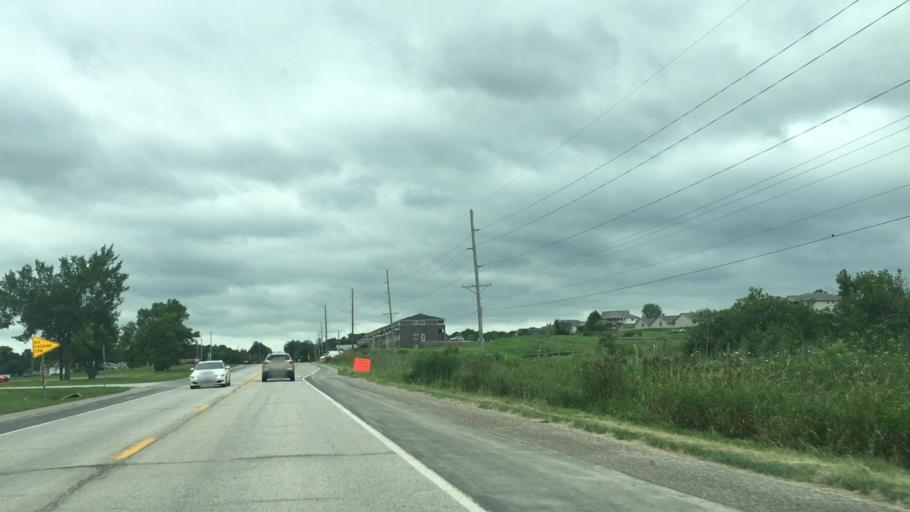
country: US
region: Iowa
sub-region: Johnson County
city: Tiffin
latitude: 41.7065
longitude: -91.6541
